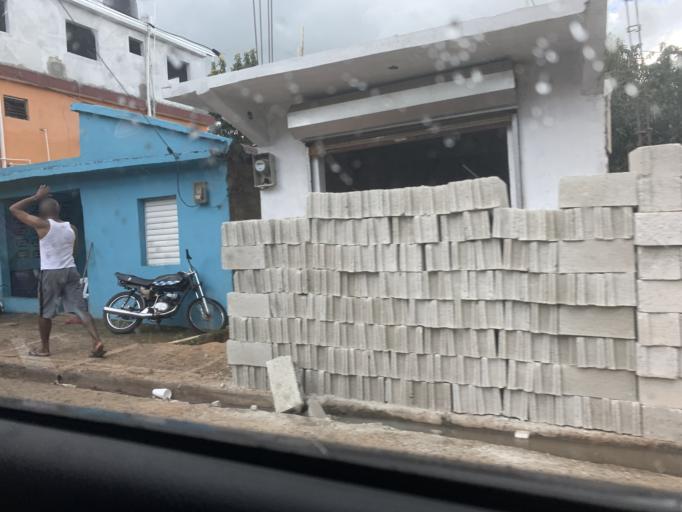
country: DO
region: Monte Plata
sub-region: Yamasa
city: Yamasa
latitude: 18.7754
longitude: -70.0276
